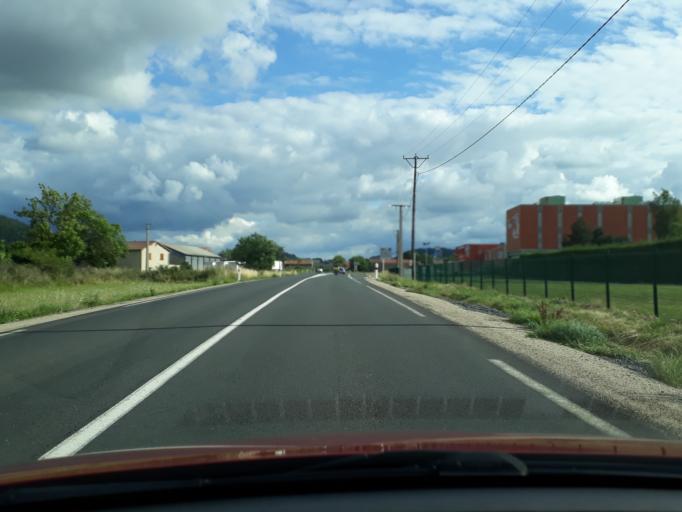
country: FR
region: Auvergne
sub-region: Departement de la Haute-Loire
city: Solignac-sur-Loire
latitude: 44.9649
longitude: 3.8446
